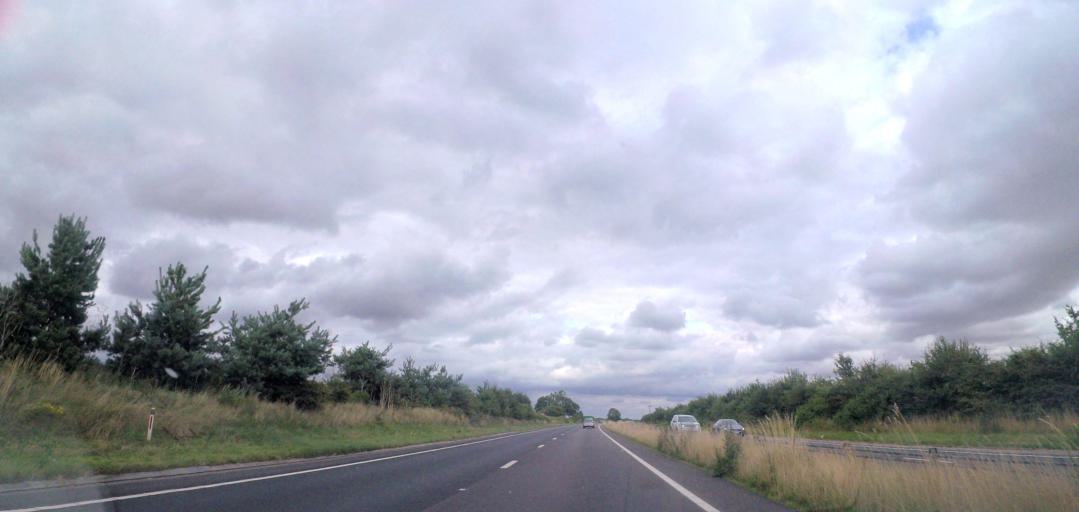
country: GB
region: England
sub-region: Norfolk
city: Snetterton
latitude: 52.4606
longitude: 0.8946
